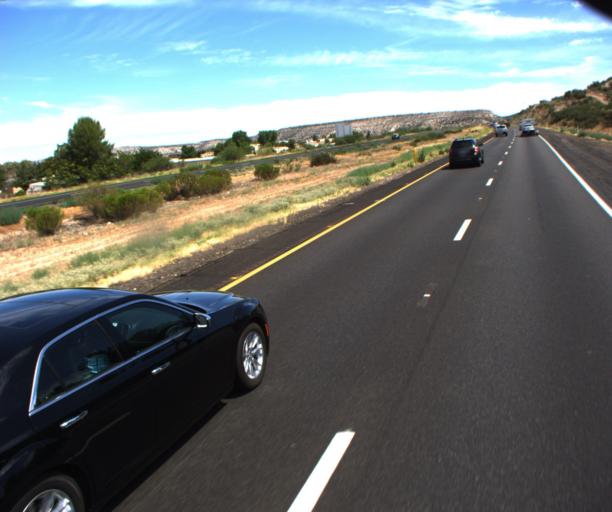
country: US
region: Arizona
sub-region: Yavapai County
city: Camp Verde
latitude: 34.6002
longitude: -111.8720
